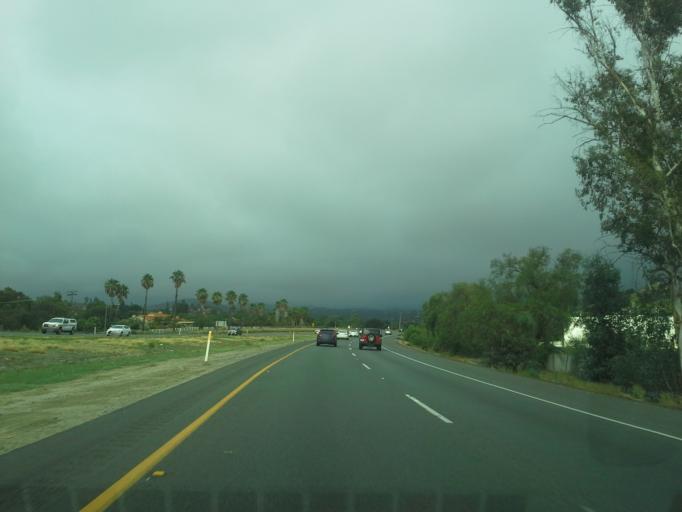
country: US
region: California
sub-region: San Diego County
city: Crest
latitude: 32.8505
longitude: -116.8705
